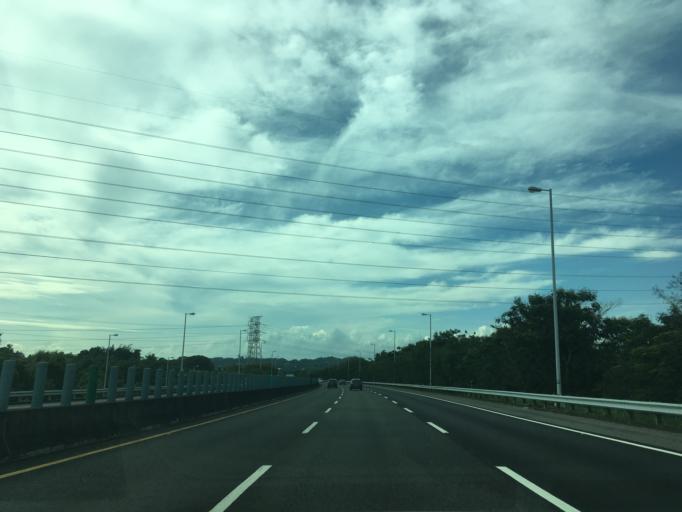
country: TW
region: Taiwan
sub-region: Chiayi
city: Jiayi Shi
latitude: 23.4997
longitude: 120.4930
